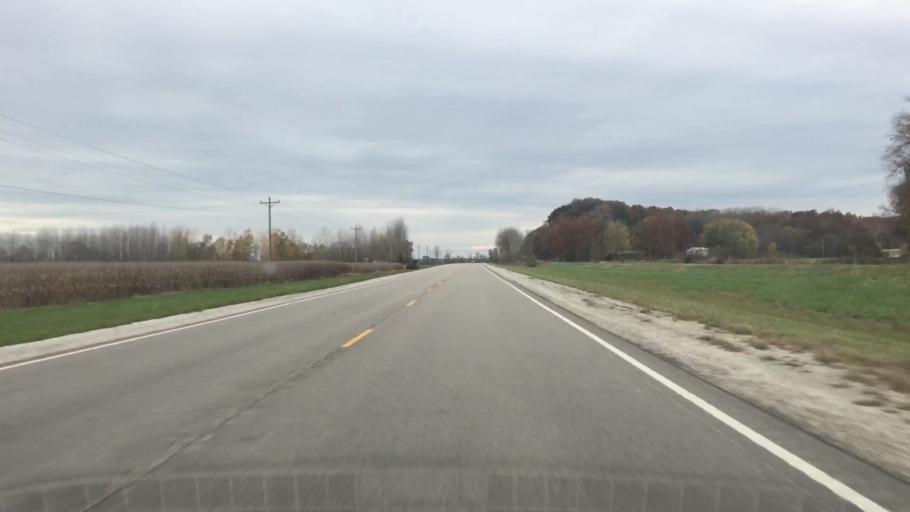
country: US
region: Missouri
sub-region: Callaway County
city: Holts Summit
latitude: 38.5820
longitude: -92.1060
